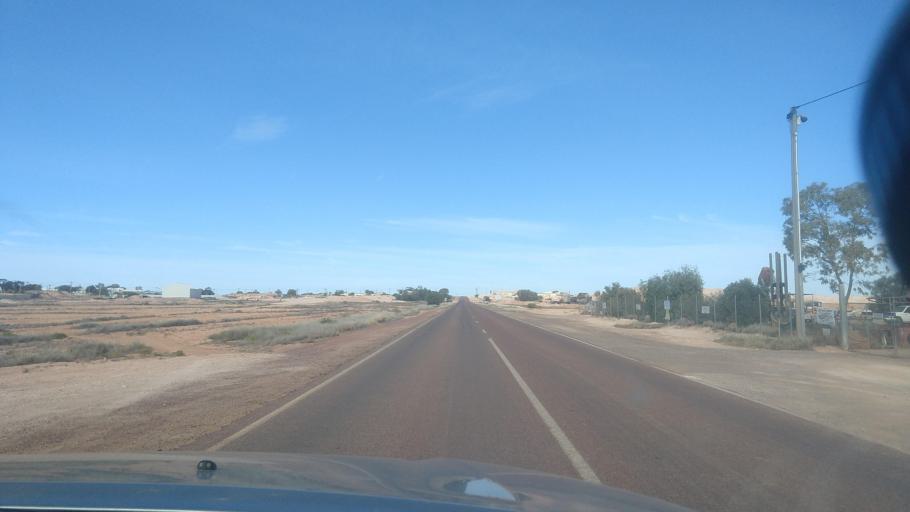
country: AU
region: South Australia
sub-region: Coober Pedy
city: Coober Pedy
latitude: -29.0147
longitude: 134.7461
